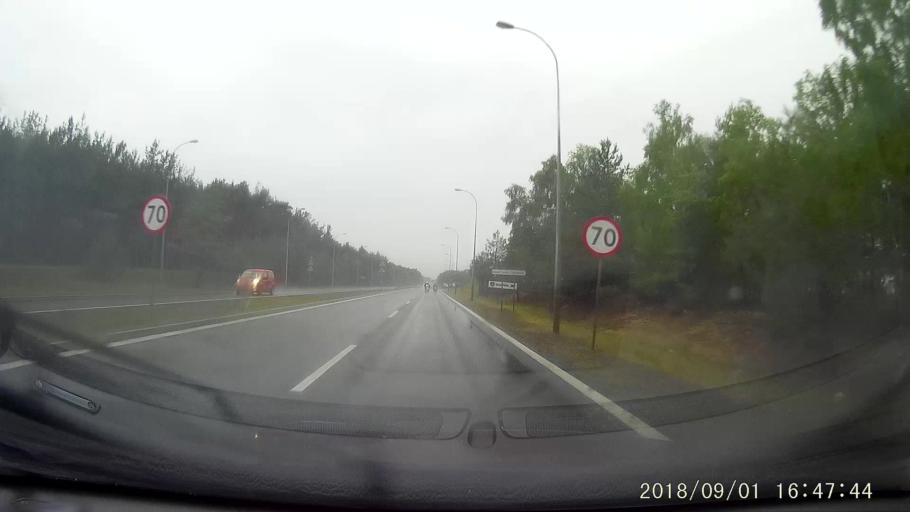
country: PL
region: Lubusz
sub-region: Zielona Gora
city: Zielona Gora
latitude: 51.9566
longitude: 15.5431
